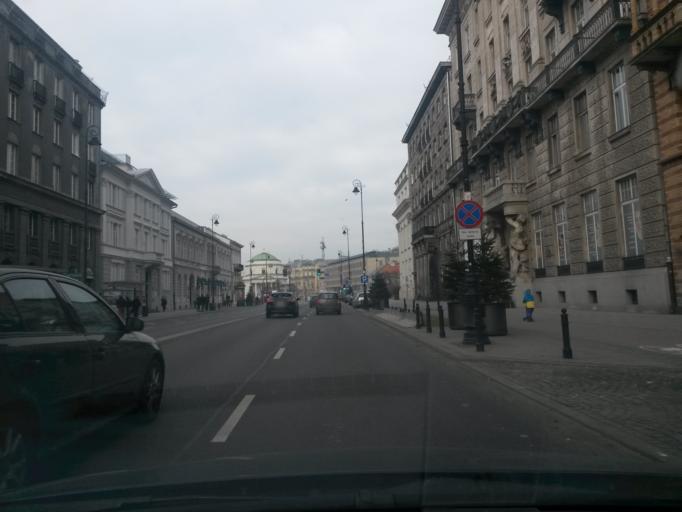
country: PL
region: Masovian Voivodeship
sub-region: Warszawa
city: Srodmiescie
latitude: 52.2267
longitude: 21.0234
